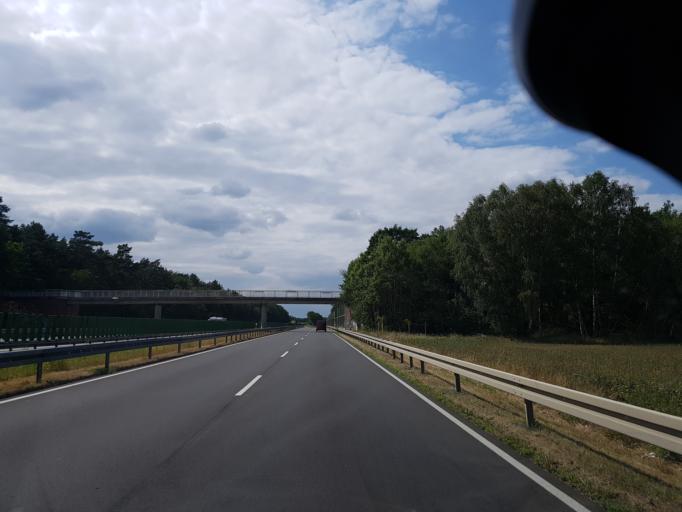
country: DE
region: Brandenburg
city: Vetschau
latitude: 51.7744
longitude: 14.0881
